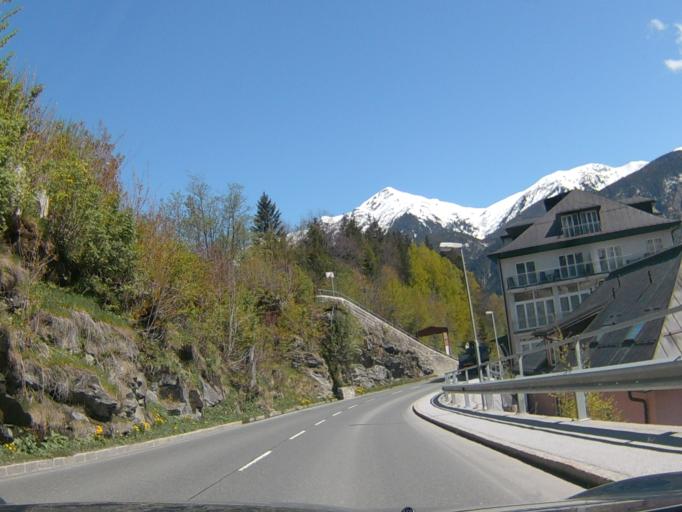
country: AT
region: Salzburg
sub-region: Politischer Bezirk Sankt Johann im Pongau
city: Bad Gastein
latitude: 47.1146
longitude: 13.1322
